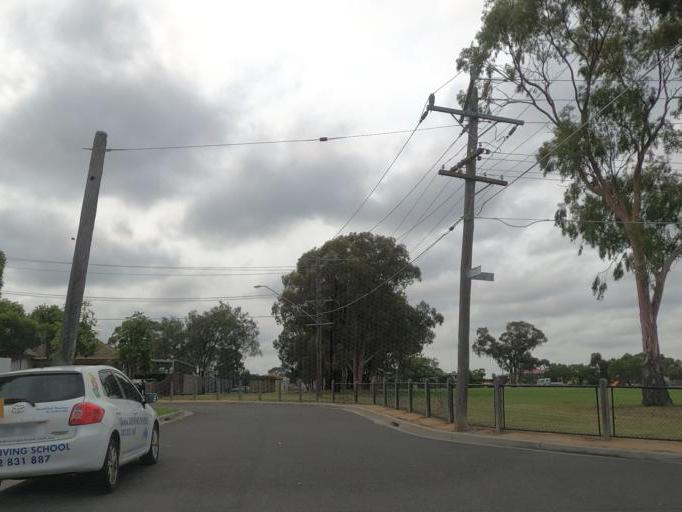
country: AU
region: Victoria
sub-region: Moreland
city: Pascoe Vale
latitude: -37.7217
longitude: 144.9374
